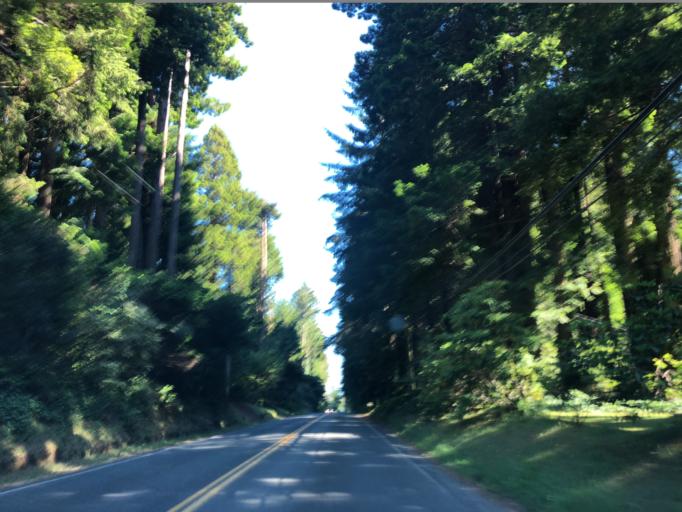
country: US
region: California
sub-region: Humboldt County
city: Westhaven-Moonstone
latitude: 41.0715
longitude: -124.1441
